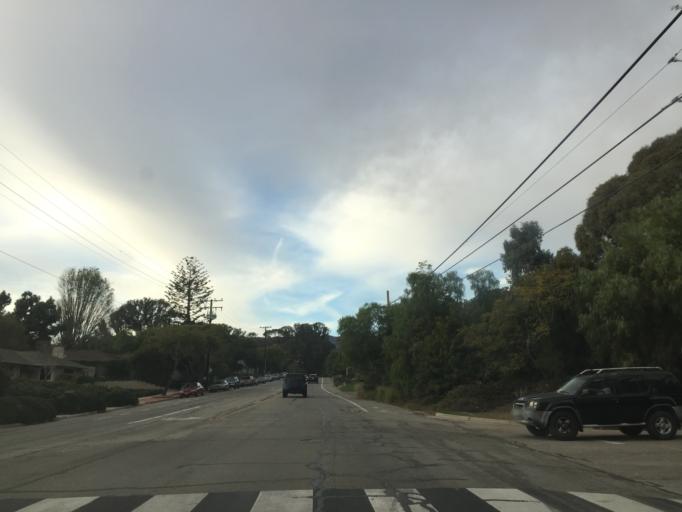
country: US
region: California
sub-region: Santa Barbara County
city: Goleta
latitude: 34.4460
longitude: -119.7897
